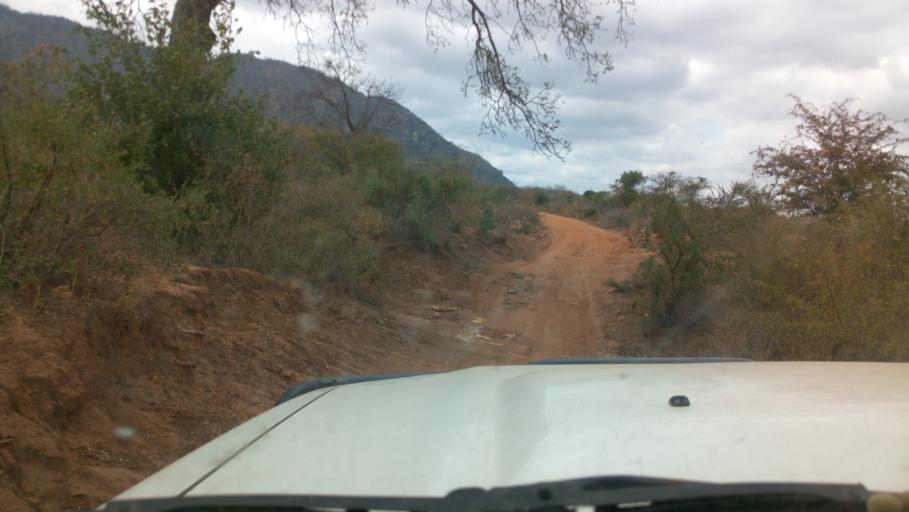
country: KE
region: Kitui
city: Kitui
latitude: -1.8857
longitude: 38.3880
